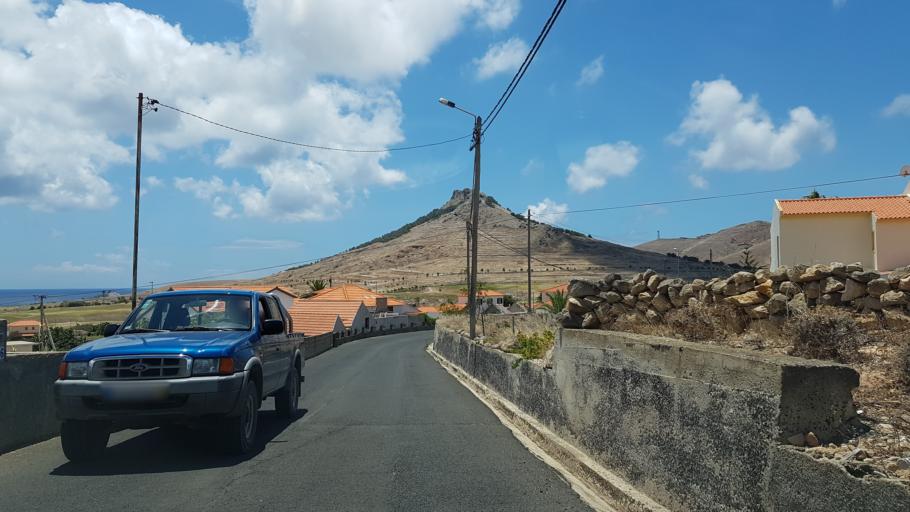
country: PT
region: Madeira
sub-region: Porto Santo
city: Vila de Porto Santo
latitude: 33.0564
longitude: -16.3614
